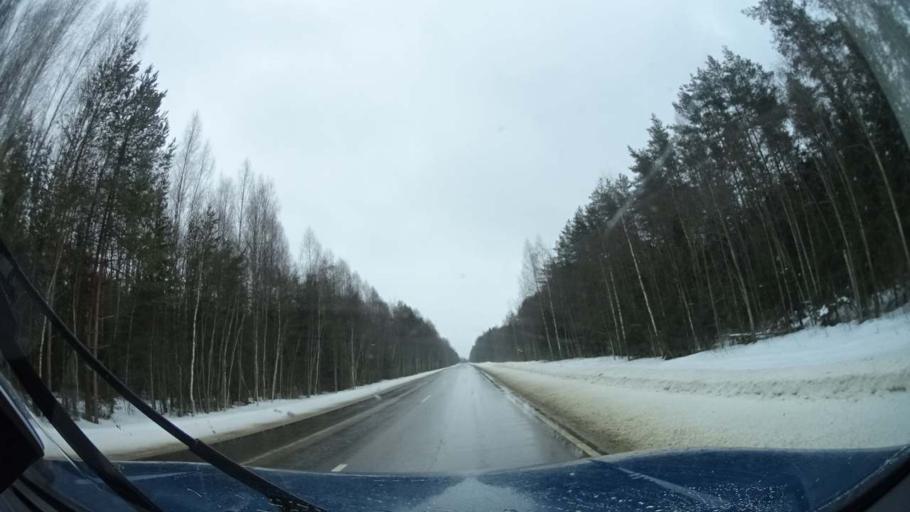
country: RU
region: Tverskaya
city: Radchenko
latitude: 56.8511
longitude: 36.5042
